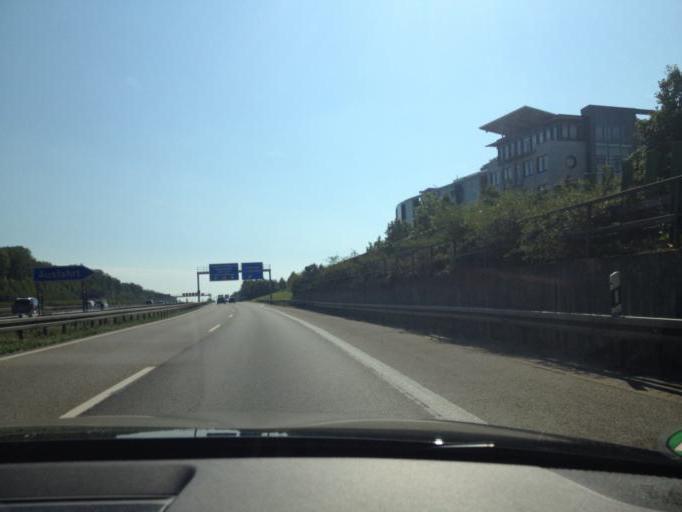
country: DE
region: Baden-Wuerttemberg
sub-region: Regierungsbezirk Stuttgart
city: Leinfelden-Echterdingen
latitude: 48.7087
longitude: 9.1462
